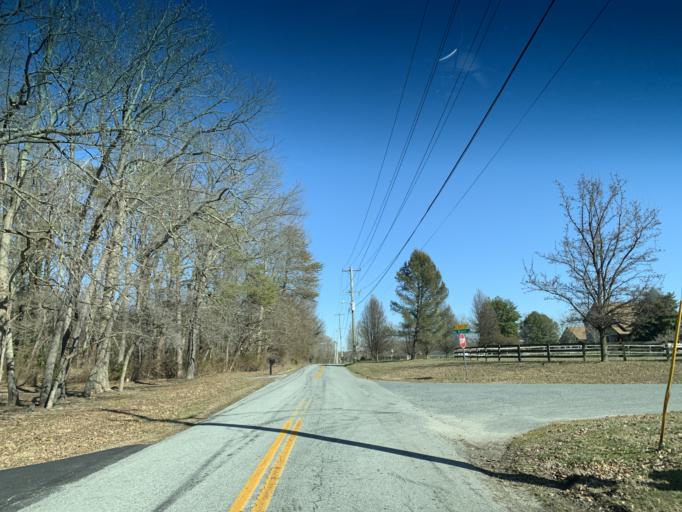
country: US
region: Maryland
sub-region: Cecil County
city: Charlestown
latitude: 39.4937
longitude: -75.9057
